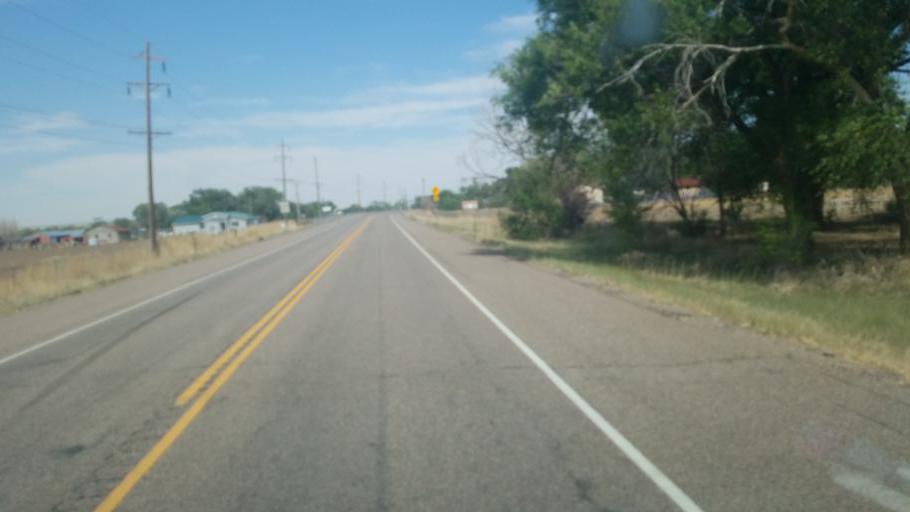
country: US
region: Colorado
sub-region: Otero County
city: Fowler
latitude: 38.2285
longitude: -104.2687
